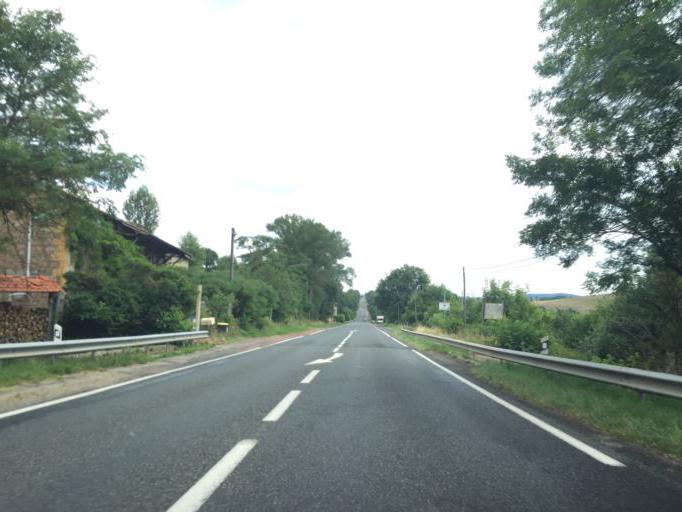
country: FR
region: Rhone-Alpes
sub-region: Departement du Rhone
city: Saint-Romain-de-Popey
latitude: 45.8650
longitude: 4.5506
